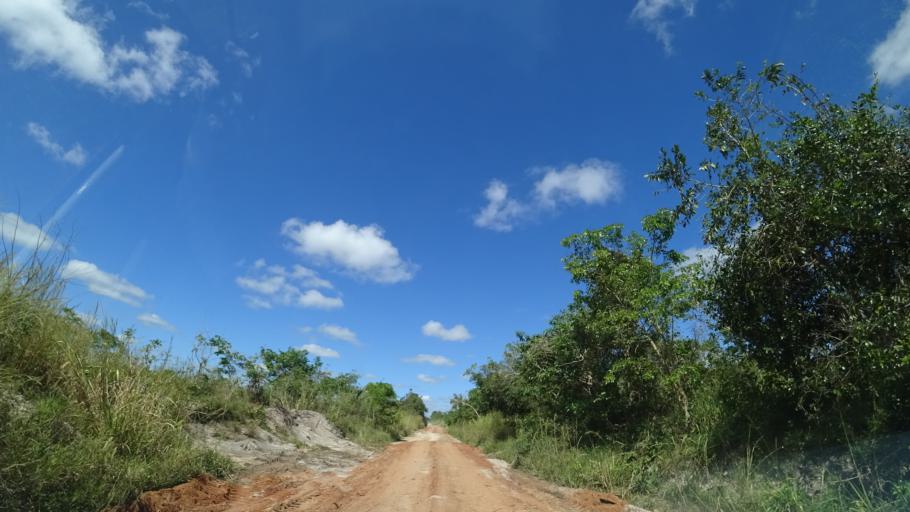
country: MZ
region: Sofala
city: Dondo
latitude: -19.3013
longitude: 34.6919
